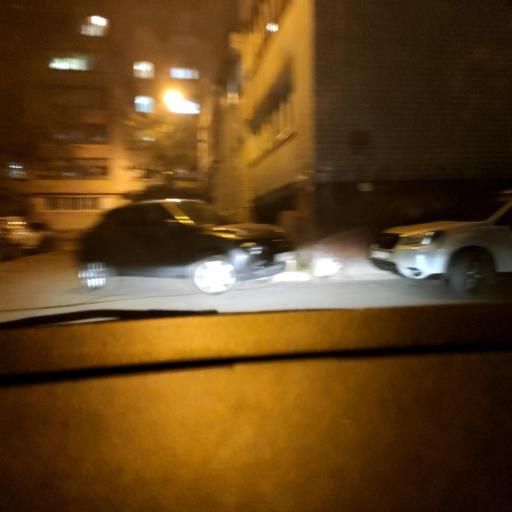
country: RU
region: Voronezj
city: Voronezh
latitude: 51.6736
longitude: 39.1576
